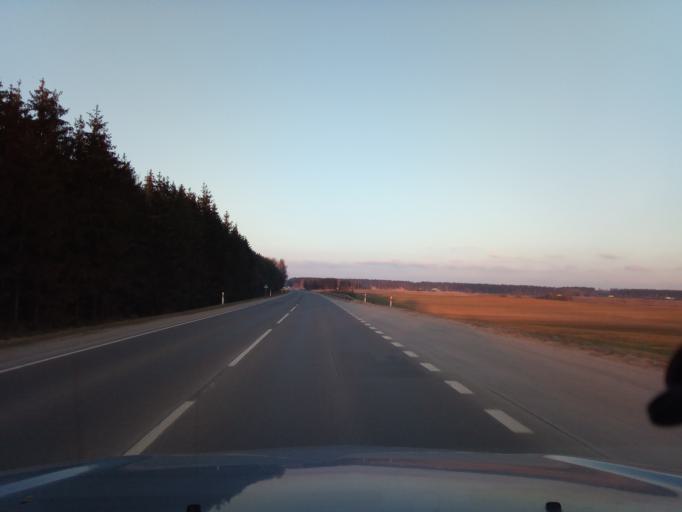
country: LT
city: Lentvaris
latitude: 54.5841
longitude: 25.0641
